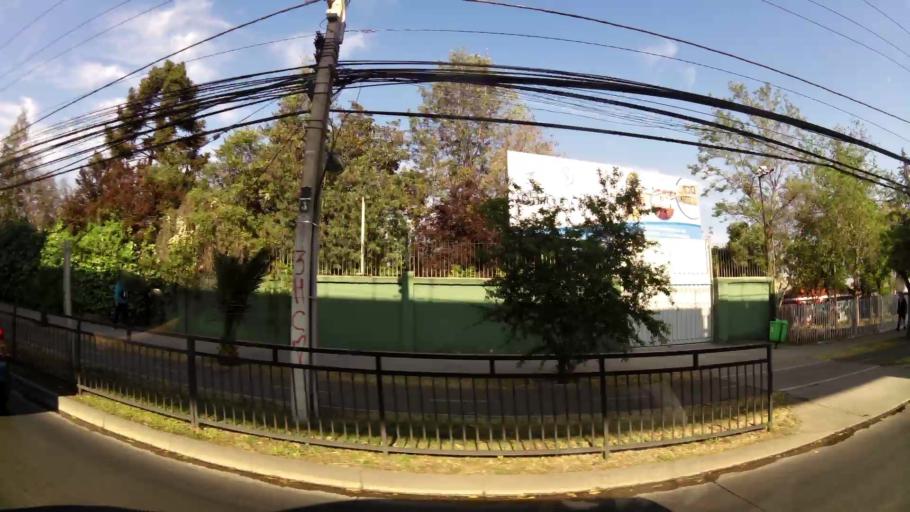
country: CL
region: Santiago Metropolitan
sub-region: Provincia de Santiago
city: La Pintana
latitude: -33.5454
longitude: -70.5886
